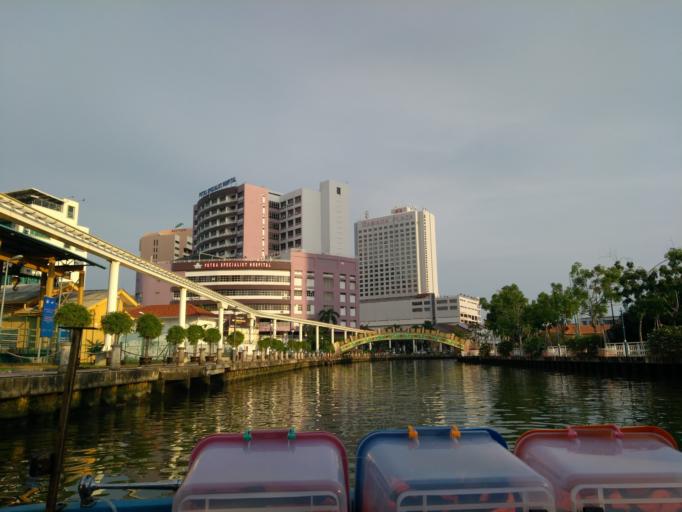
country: MY
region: Melaka
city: Malacca
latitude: 2.2037
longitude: 102.2515
